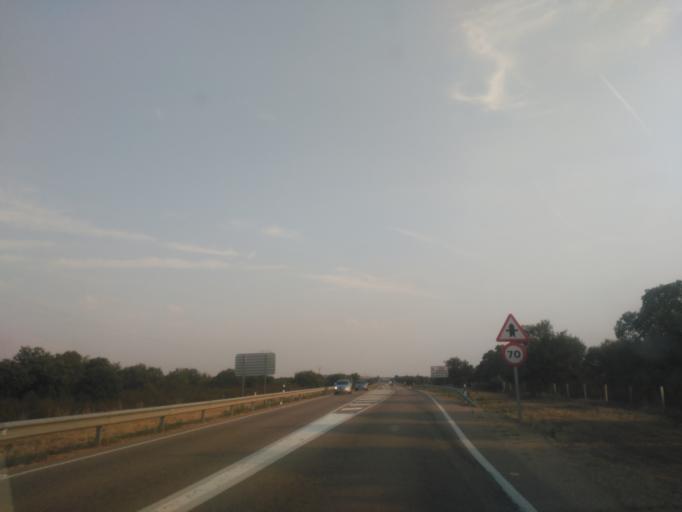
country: ES
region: Castille and Leon
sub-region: Provincia de Zamora
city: San Cebrian de Castro
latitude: 41.7187
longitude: -5.8101
